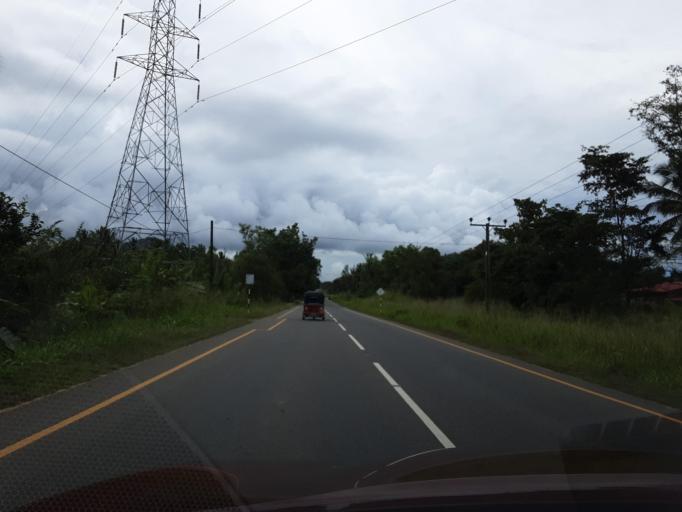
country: LK
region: Uva
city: Badulla
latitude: 7.3903
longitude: 81.1373
